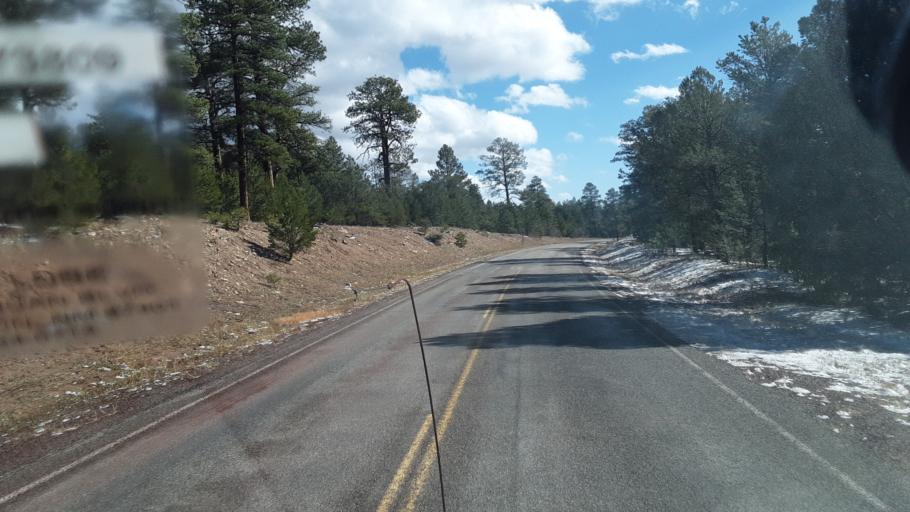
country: US
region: New Mexico
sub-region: Rio Arriba County
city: Santa Teresa
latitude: 36.1984
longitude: -106.7498
